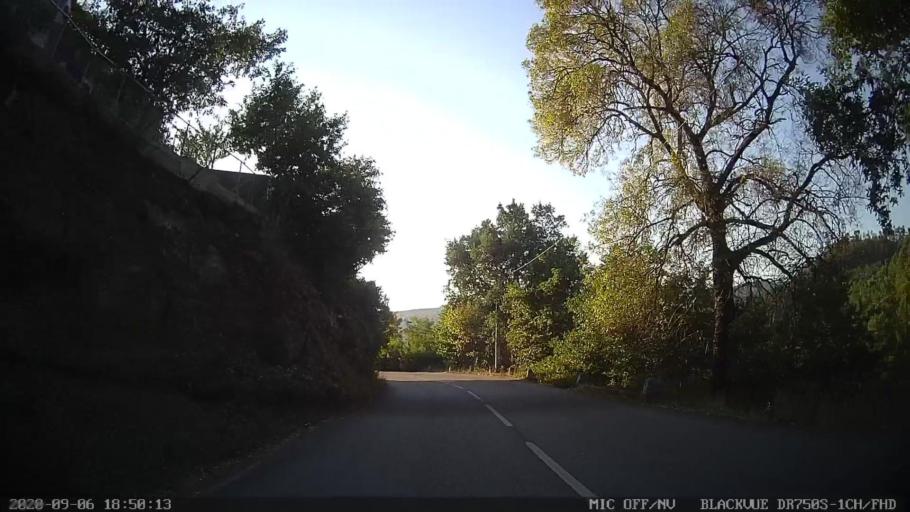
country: PT
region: Porto
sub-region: Amarante
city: Amarante
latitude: 41.2628
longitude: -7.9958
